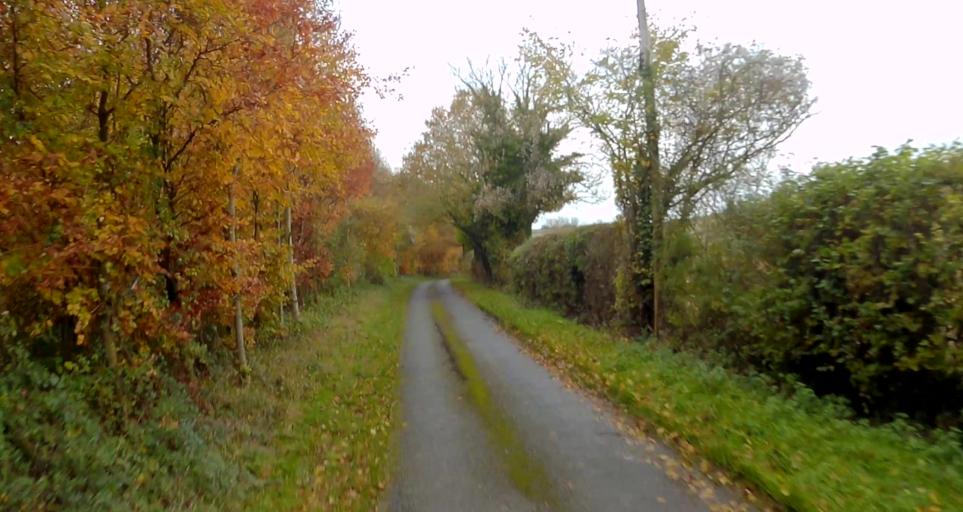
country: GB
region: England
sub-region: Hampshire
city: Long Sutton
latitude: 51.2393
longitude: -0.8888
